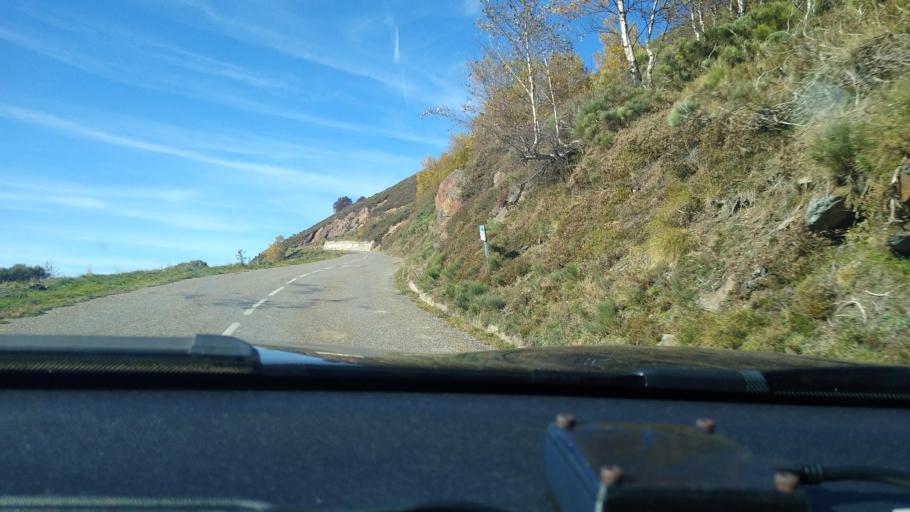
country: FR
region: Midi-Pyrenees
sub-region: Departement de l'Ariege
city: Ax-les-Thermes
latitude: 42.7278
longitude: 1.9638
